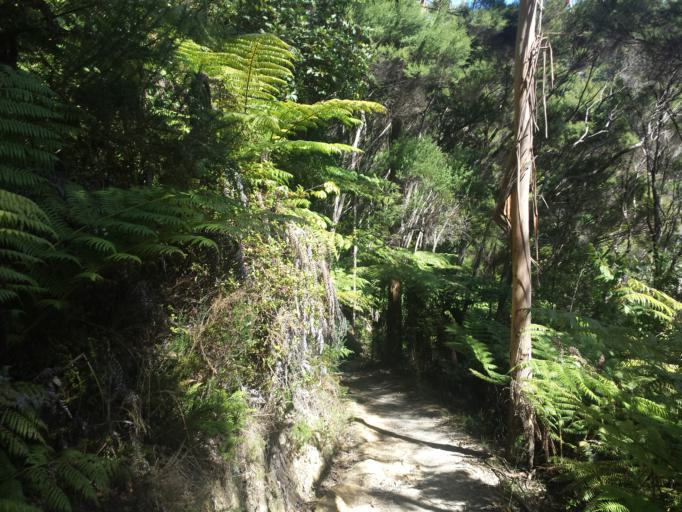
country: NZ
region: Northland
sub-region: Far North District
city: Paihia
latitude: -35.3030
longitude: 174.1056
